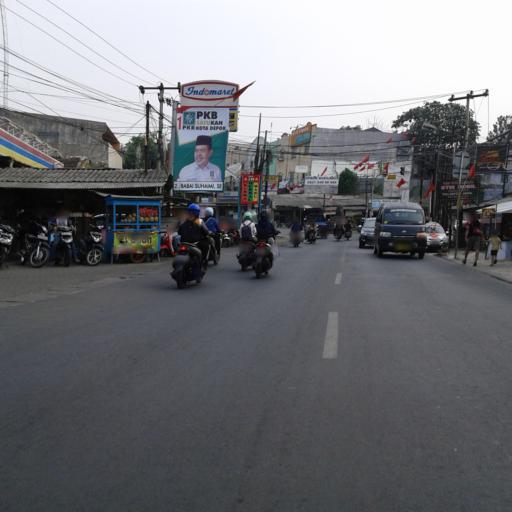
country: ID
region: West Java
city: Sawangan
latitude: -6.4027
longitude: 106.7709
